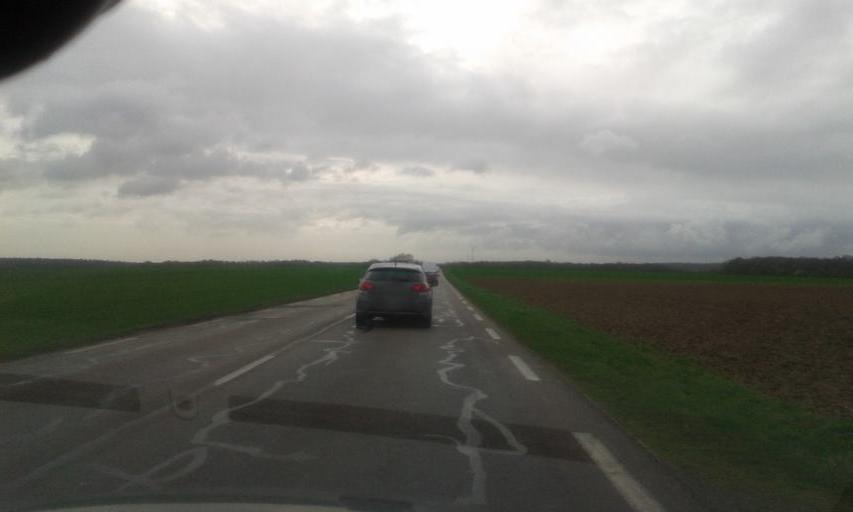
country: FR
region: Haute-Normandie
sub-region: Departement de l'Eure
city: Fleury-sur-Andelle
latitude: 49.3808
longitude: 1.3200
